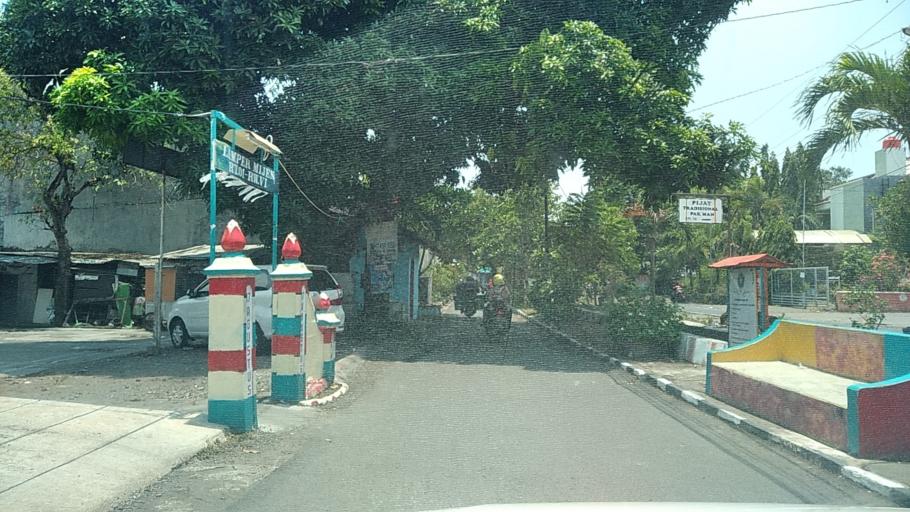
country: ID
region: Central Java
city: Semarang
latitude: -7.0030
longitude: 110.4431
